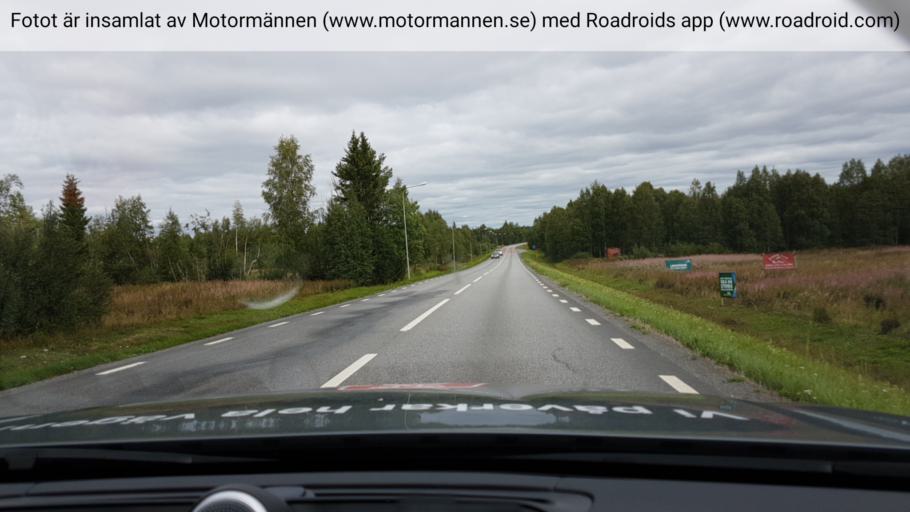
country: SE
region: Jaemtland
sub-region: Stroemsunds Kommun
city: Stroemsund
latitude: 63.8304
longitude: 15.5122
